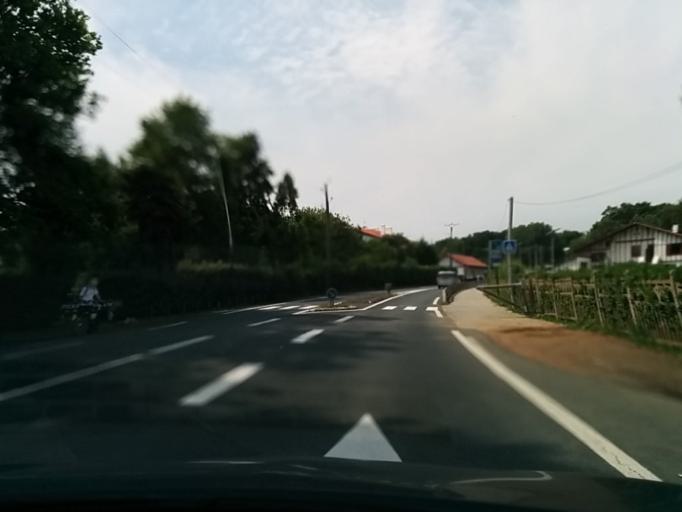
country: FR
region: Aquitaine
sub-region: Departement des Pyrenees-Atlantiques
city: Urrugne
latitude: 43.3795
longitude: -1.7329
